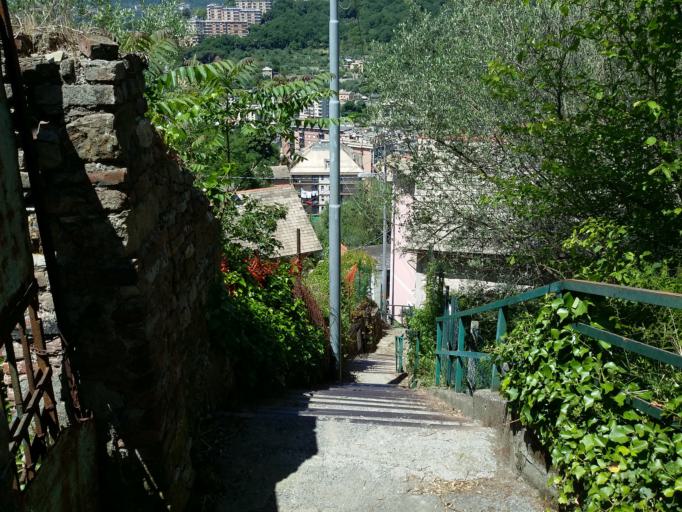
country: IT
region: Liguria
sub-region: Provincia di Genova
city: Genoa
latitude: 44.4176
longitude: 8.9724
